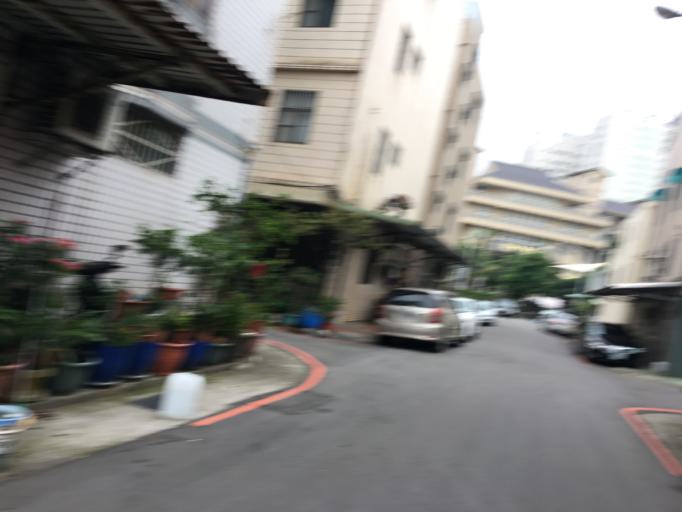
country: TW
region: Taiwan
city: Taoyuan City
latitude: 25.0191
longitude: 121.3066
